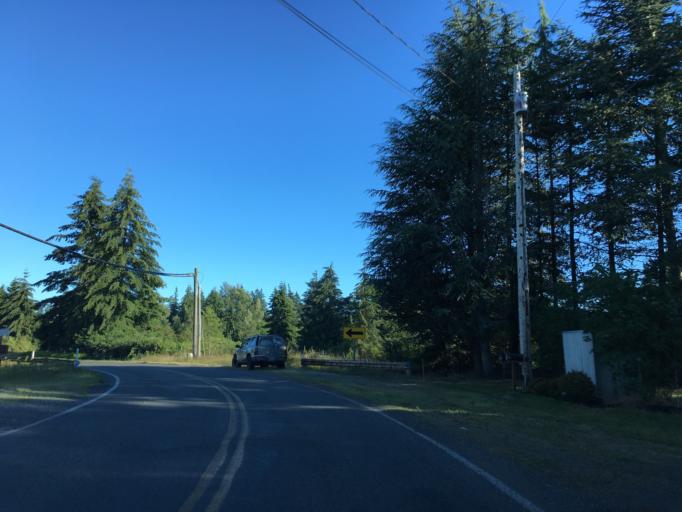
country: US
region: Washington
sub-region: Whatcom County
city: Ferndale
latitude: 48.9240
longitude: -122.6385
